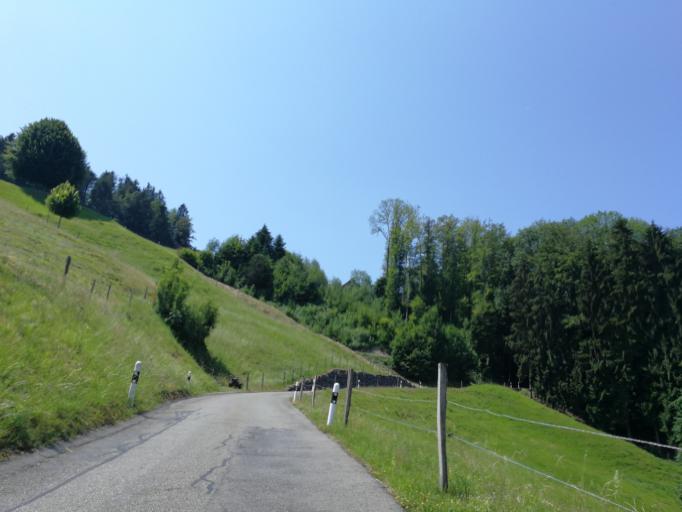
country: CH
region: Schwyz
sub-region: Bezirk March
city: Altendorf
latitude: 47.1875
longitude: 8.8094
